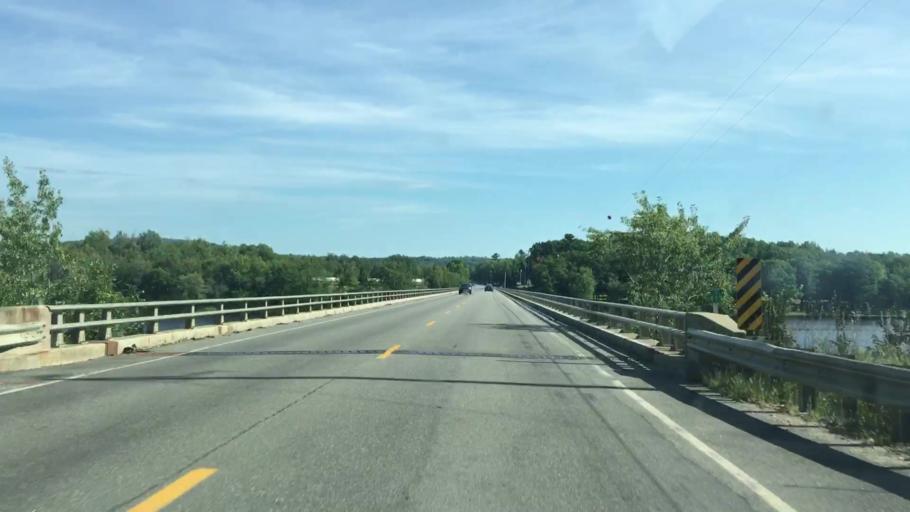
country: US
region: Maine
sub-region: Penobscot County
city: Lincoln
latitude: 45.3638
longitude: -68.5491
